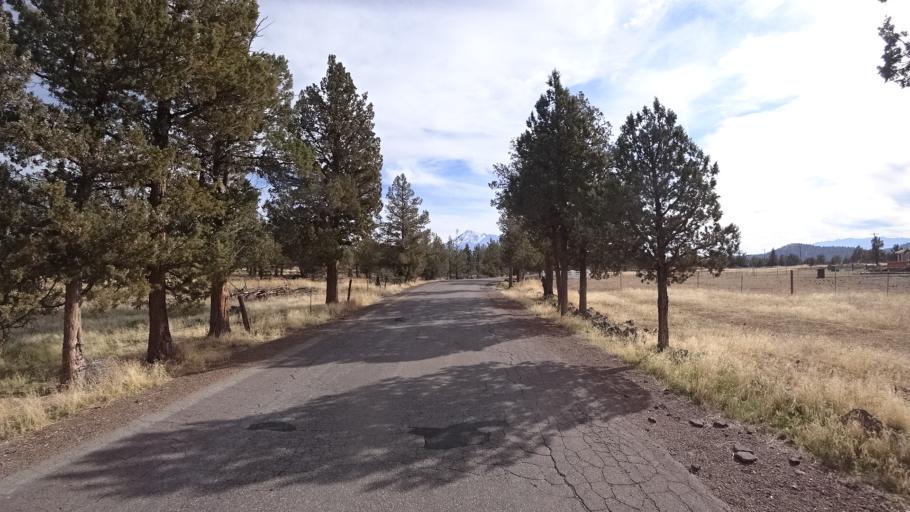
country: US
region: California
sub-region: Siskiyou County
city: Weed
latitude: 41.5931
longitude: -122.4017
